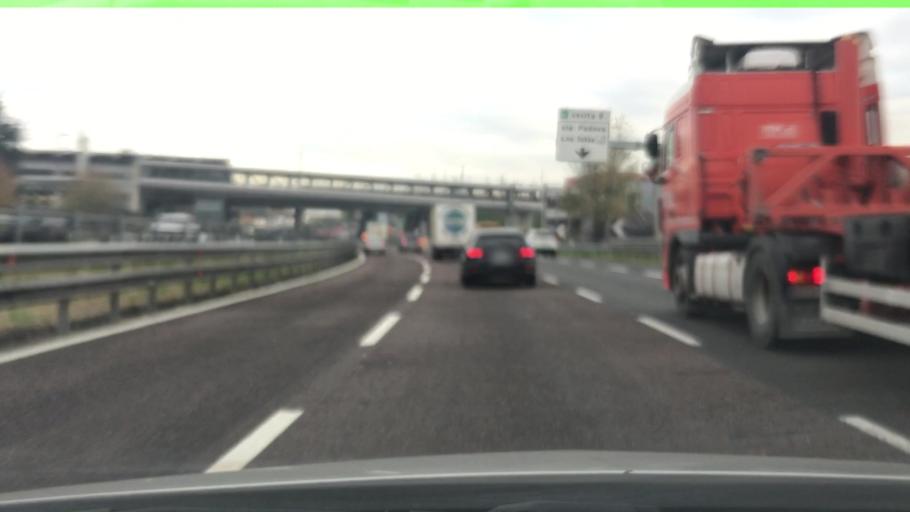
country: IT
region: Lombardy
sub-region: Citta metropolitana di Milano
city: Cologno Monzese
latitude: 45.5095
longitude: 9.2620
